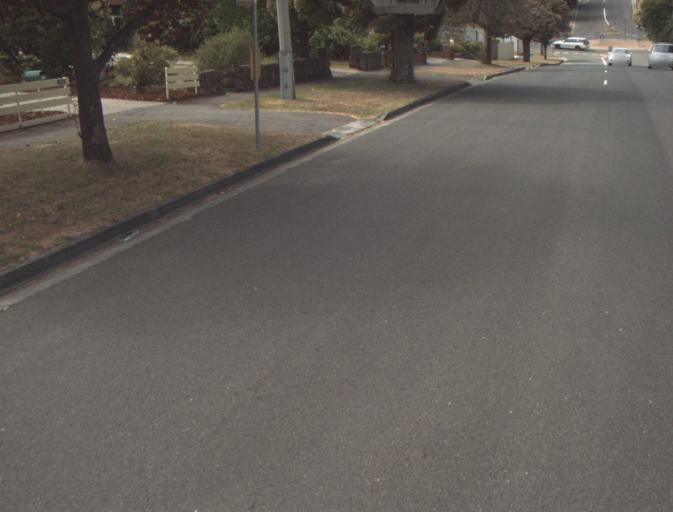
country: AU
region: Tasmania
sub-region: Launceston
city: West Launceston
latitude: -41.4588
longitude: 147.1278
